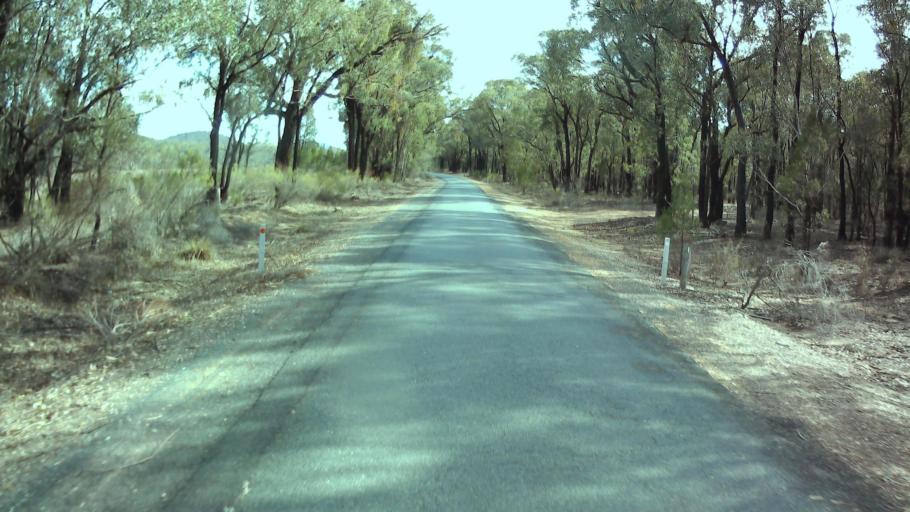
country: AU
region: New South Wales
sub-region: Weddin
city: Grenfell
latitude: -33.8608
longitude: 148.2143
